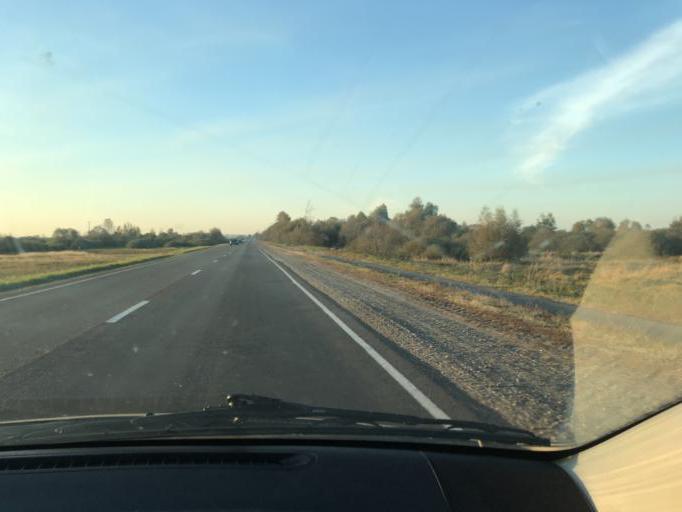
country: BY
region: Brest
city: Pinsk
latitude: 52.0831
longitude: 26.1391
